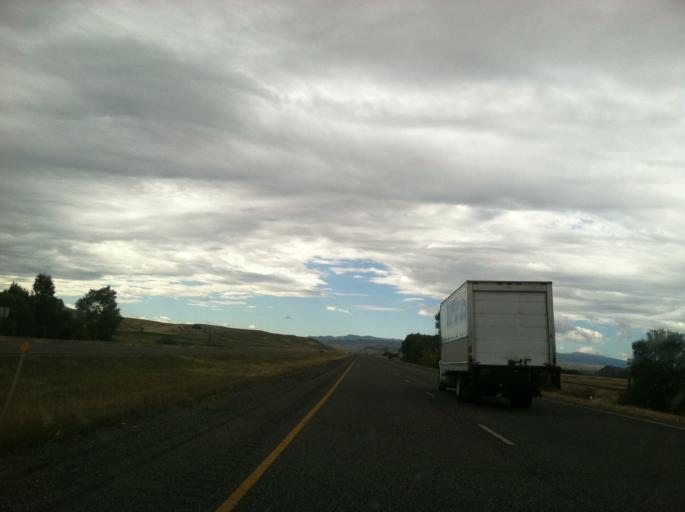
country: US
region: Montana
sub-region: Park County
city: Livingston
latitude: 45.7136
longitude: -110.4061
